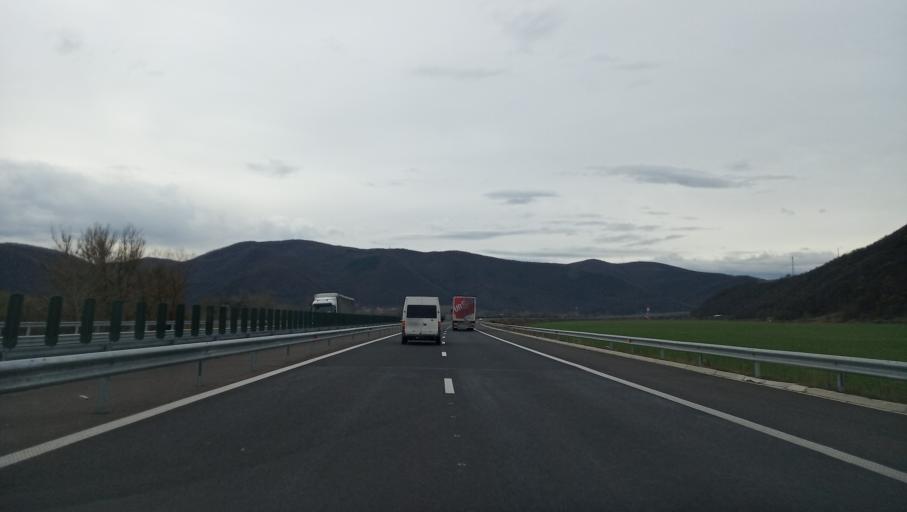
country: RO
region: Hunedoara
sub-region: Comuna Vetel
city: Vetel
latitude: 45.9159
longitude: 22.8119
